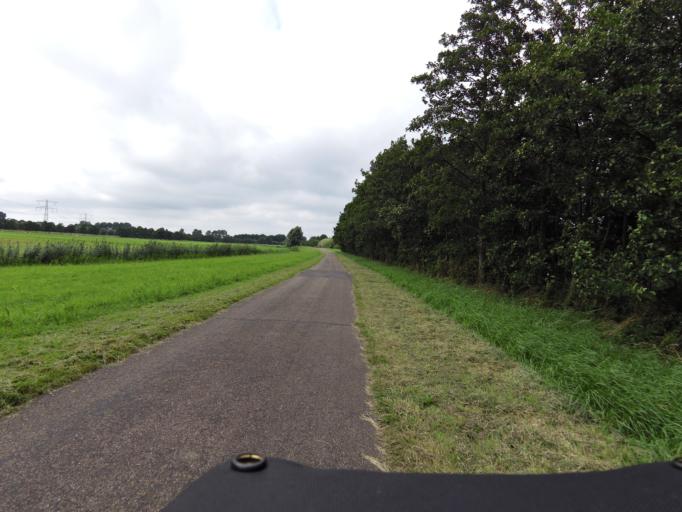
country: NL
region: South Holland
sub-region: Gemeente Spijkenisse
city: Spijkenisse
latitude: 51.8427
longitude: 4.2590
